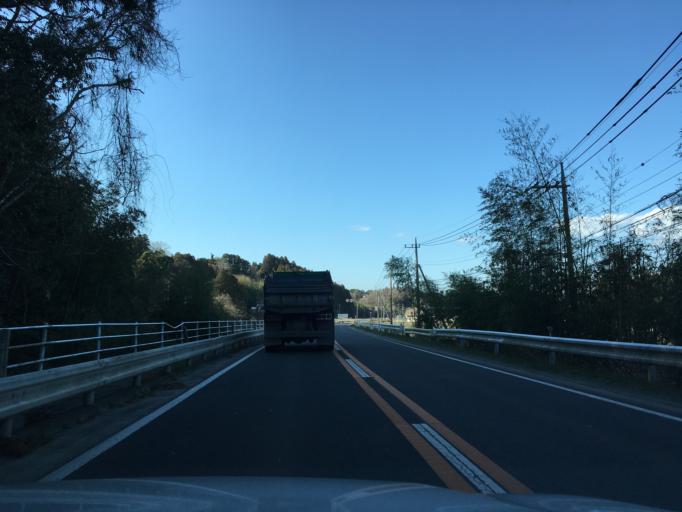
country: JP
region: Ibaraki
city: Omiya
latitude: 36.6053
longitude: 140.3992
